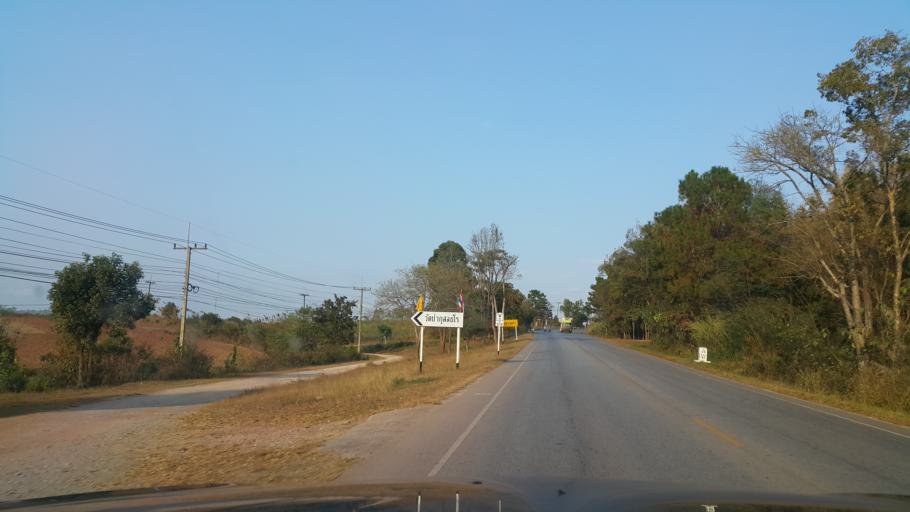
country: TH
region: Loei
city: Phu Ruea
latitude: 17.4638
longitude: 101.5133
